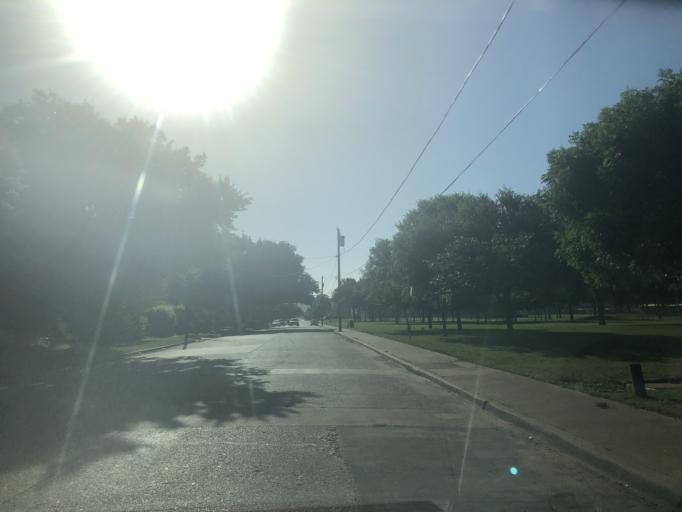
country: US
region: Texas
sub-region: Dallas County
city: Dallas
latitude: 32.7887
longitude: -96.8557
